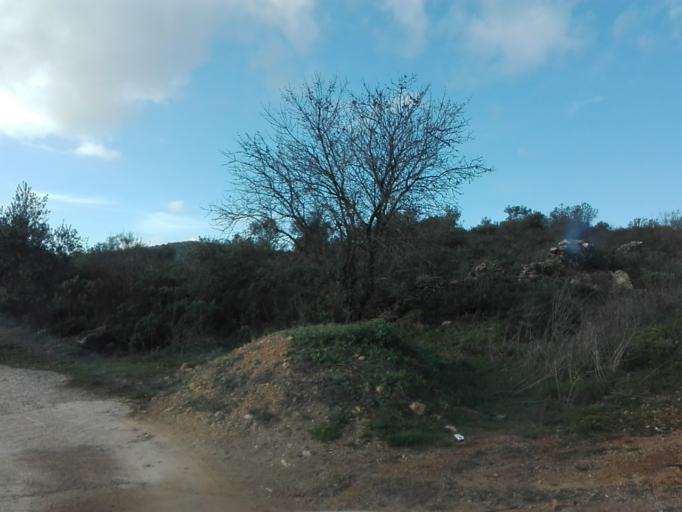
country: ES
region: Extremadura
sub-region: Provincia de Badajoz
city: Trasierra
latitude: 38.1991
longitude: -5.9910
